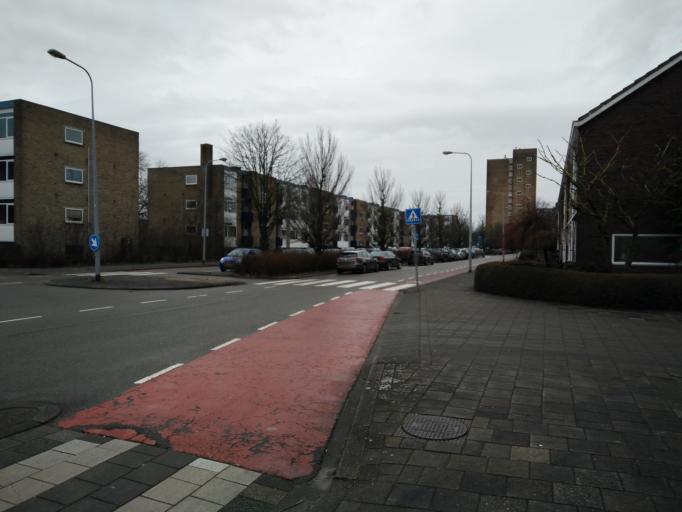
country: NL
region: Groningen
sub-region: Gemeente Groningen
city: Korrewegwijk
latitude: 53.2310
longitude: 6.5543
